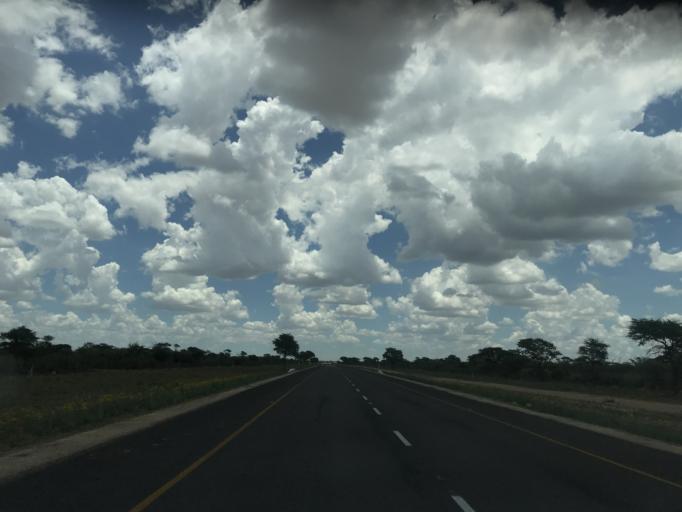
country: BW
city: Mabuli
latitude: -25.8027
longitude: 24.8413
